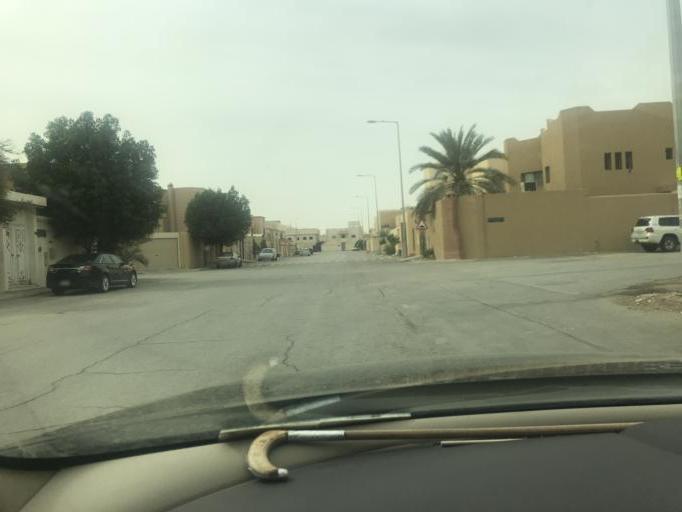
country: SA
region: Ar Riyad
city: Riyadh
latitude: 24.7539
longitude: 46.7635
